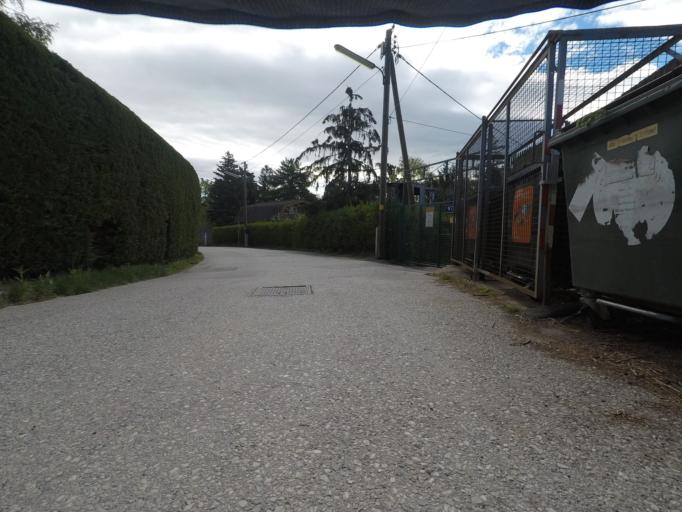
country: AT
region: Lower Austria
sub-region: Politischer Bezirk Modling
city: Perchtoldsdorf
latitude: 48.1744
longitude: 16.2554
